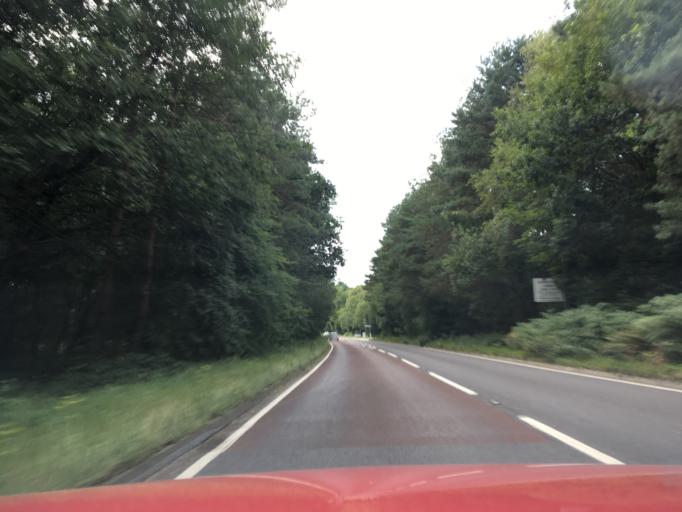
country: GB
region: England
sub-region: West Sussex
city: Midhurst
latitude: 50.9920
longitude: -0.7794
